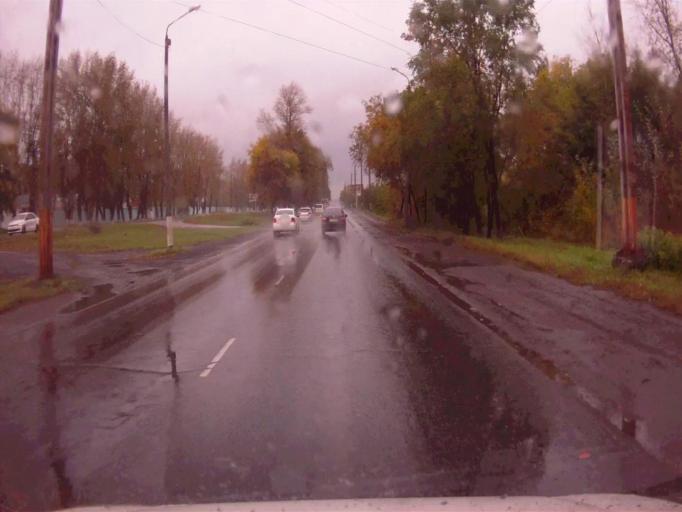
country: RU
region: Chelyabinsk
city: Dolgoderevenskoye
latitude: 55.2489
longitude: 61.3572
